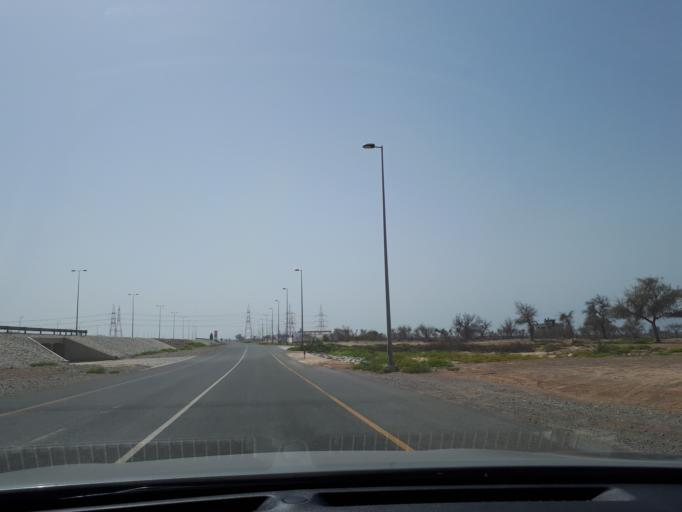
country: OM
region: Al Batinah
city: Barka'
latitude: 23.6991
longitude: 58.0117
